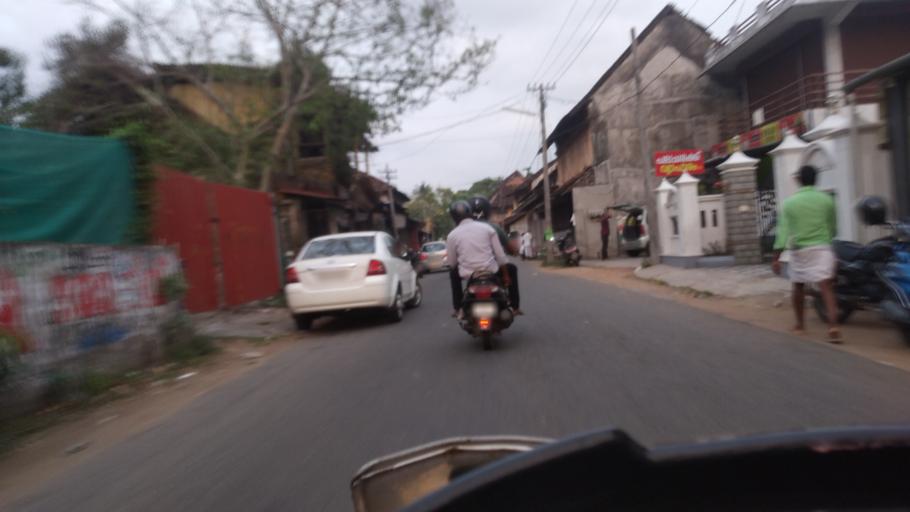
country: IN
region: Kerala
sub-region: Thrissur District
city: Kodungallur
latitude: 10.1512
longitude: 76.2211
